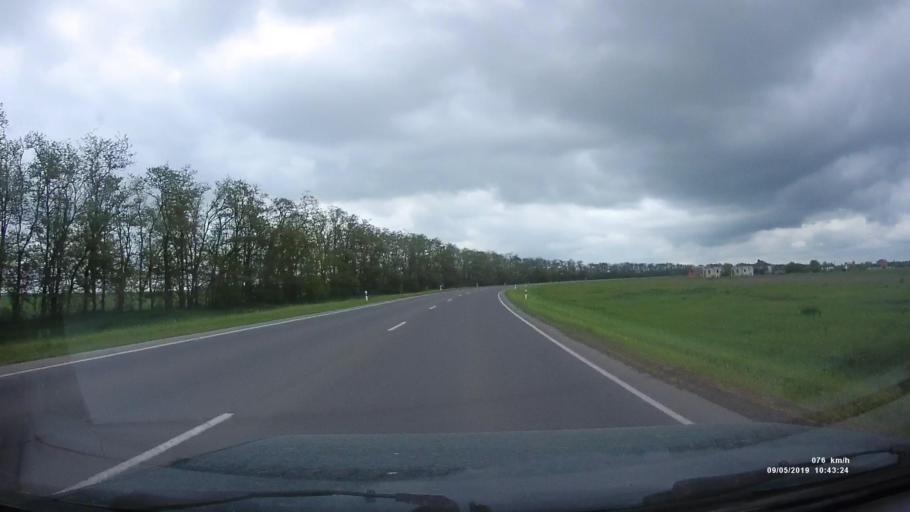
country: RU
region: Rostov
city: Peshkovo
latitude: 47.0085
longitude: 39.4035
